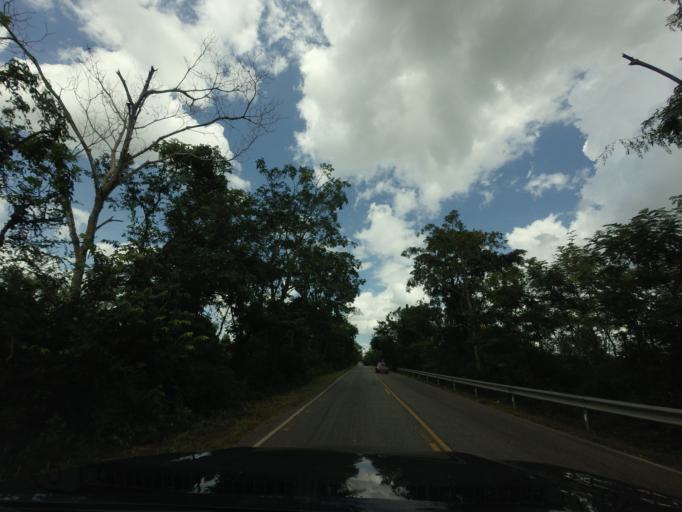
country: TH
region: Changwat Udon Thani
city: Phibun Rak
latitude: 17.6106
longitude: 103.0787
